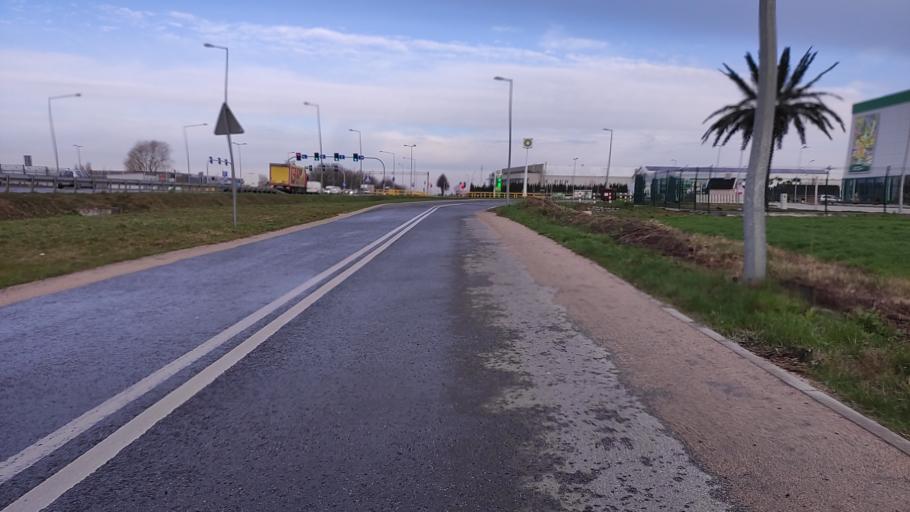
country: PL
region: Greater Poland Voivodeship
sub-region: Powiat poznanski
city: Swarzedz
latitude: 52.4026
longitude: 17.1250
